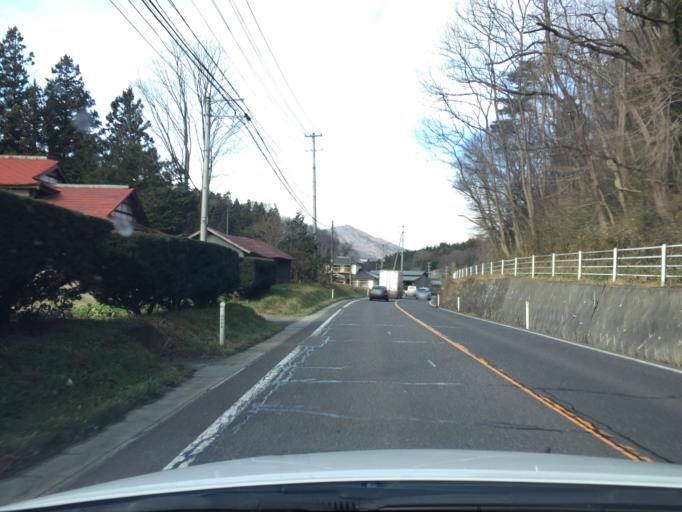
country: JP
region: Fukushima
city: Ishikawa
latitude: 37.2313
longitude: 140.5783
